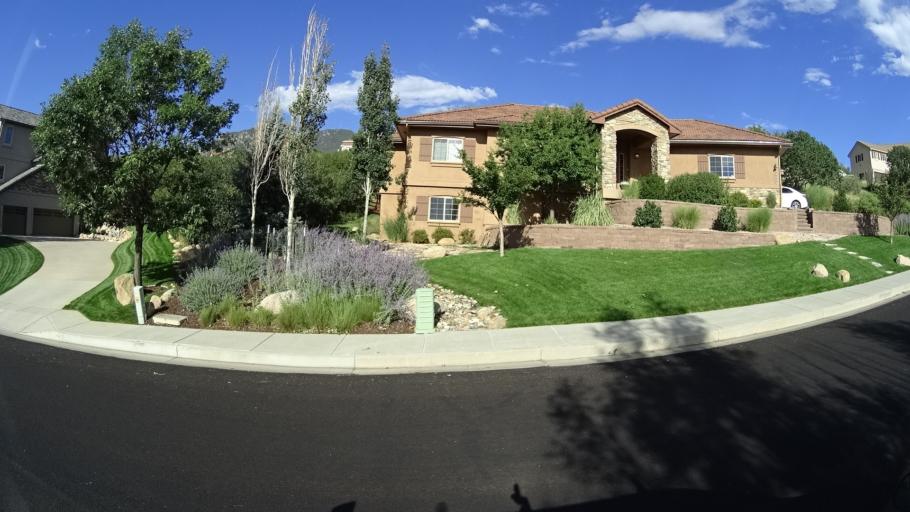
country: US
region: Colorado
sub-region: El Paso County
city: Fort Carson
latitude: 38.7583
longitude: -104.8177
